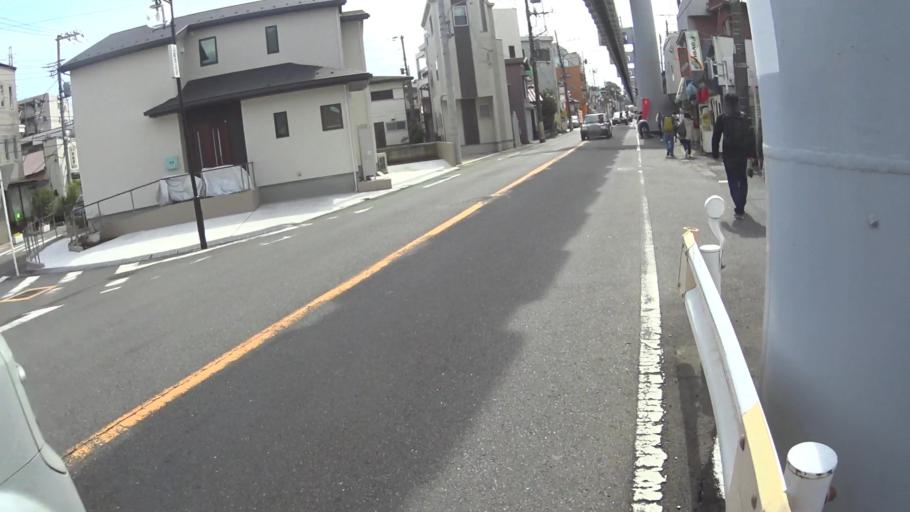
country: JP
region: Kanagawa
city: Kamakura
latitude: 35.3445
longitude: 139.5284
